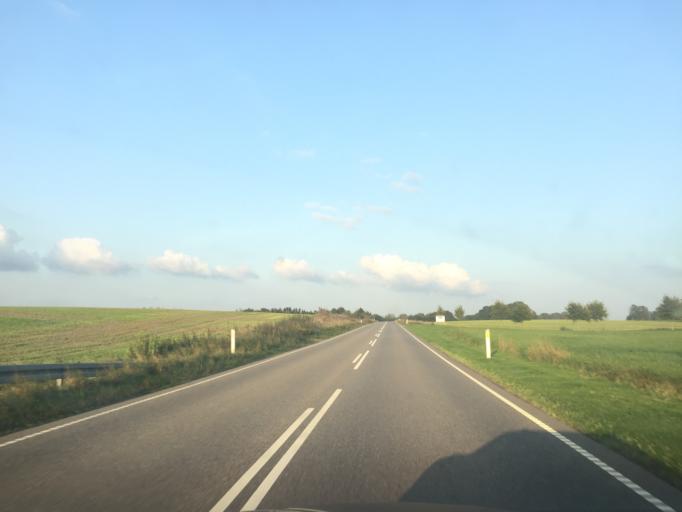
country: DK
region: Zealand
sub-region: Holbaek Kommune
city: Tollose
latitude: 55.5520
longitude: 11.7507
